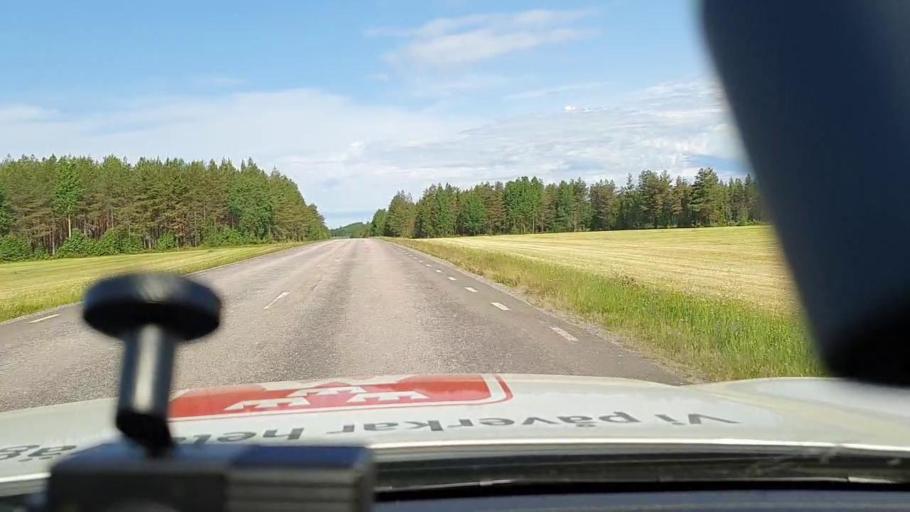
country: SE
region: Norrbotten
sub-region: Bodens Kommun
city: Boden
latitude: 65.9056
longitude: 21.3626
